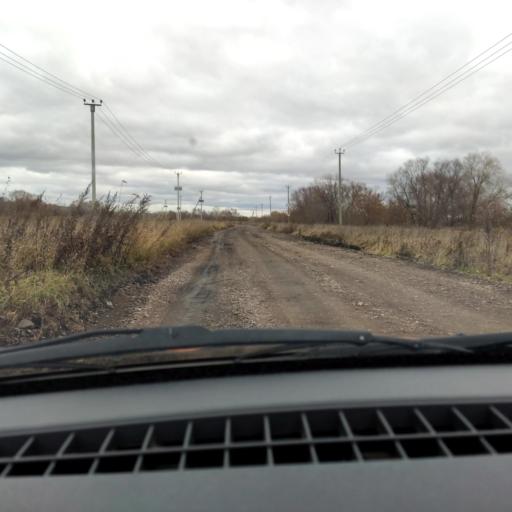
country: RU
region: Bashkortostan
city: Avdon
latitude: 54.4992
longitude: 55.8719
